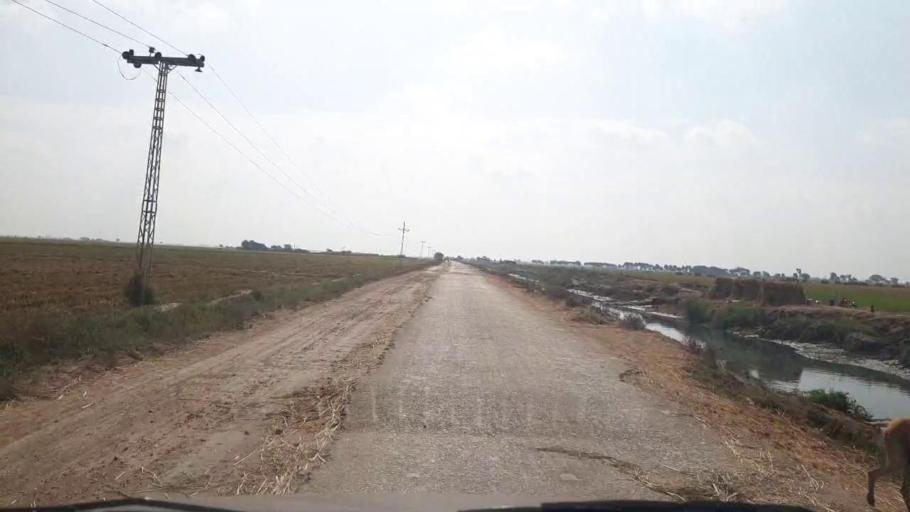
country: PK
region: Sindh
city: Kario
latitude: 24.6322
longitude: 68.5501
